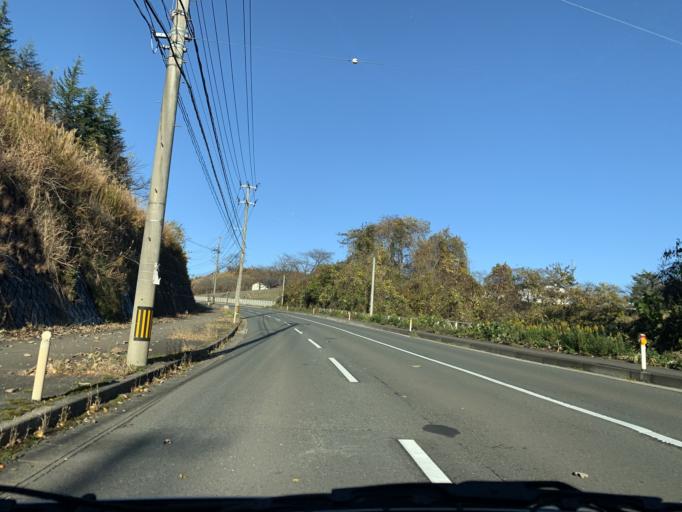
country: JP
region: Iwate
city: Mizusawa
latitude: 39.2025
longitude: 141.1768
